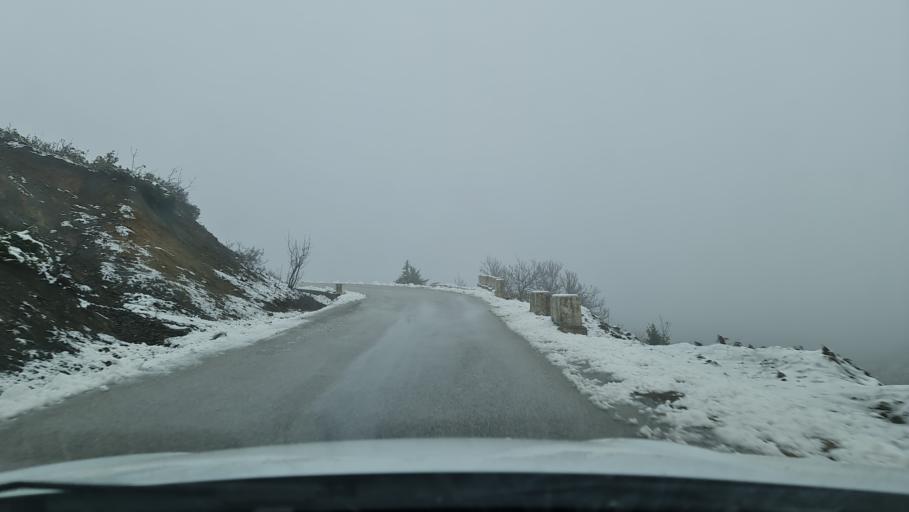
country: AL
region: Kukes
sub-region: Rrethi i Kukesit
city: Kolsh
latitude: 42.0810
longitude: 20.2953
